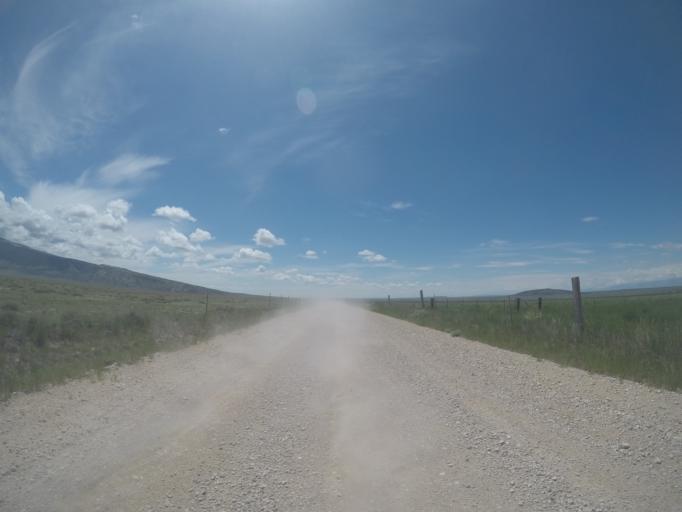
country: US
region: Montana
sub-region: Yellowstone County
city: Laurel
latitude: 45.2270
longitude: -108.6995
